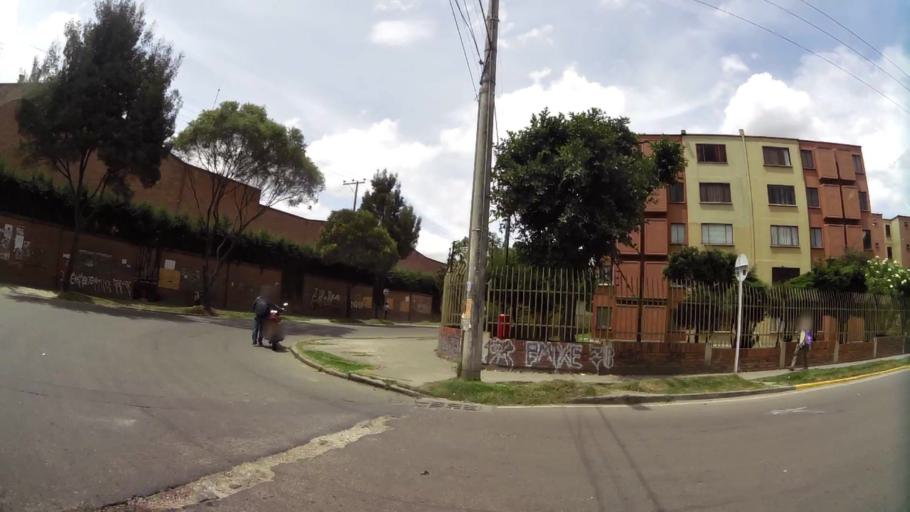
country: CO
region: Bogota D.C.
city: Bogota
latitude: 4.6493
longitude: -74.1337
